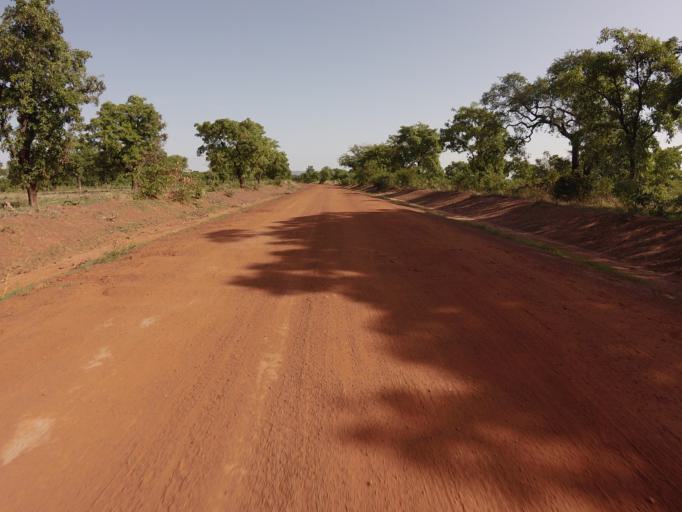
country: GH
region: Upper East
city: Bawku
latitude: 10.7471
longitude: -0.2004
